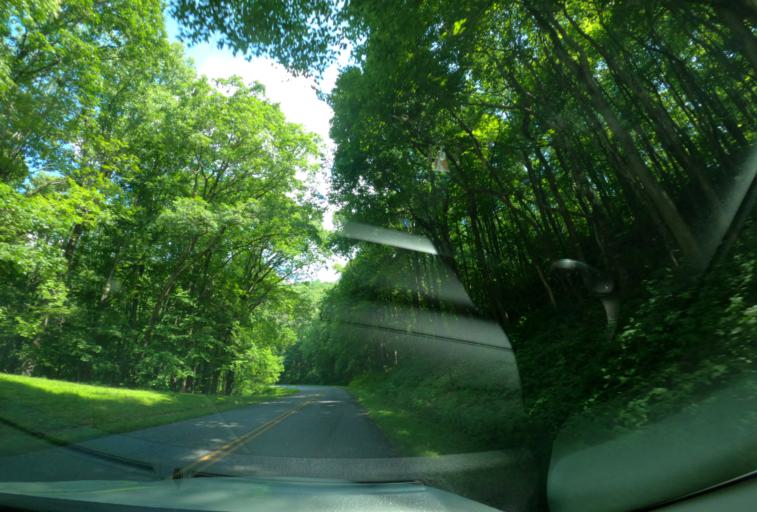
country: US
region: North Carolina
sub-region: Haywood County
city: Maggie Valley
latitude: 35.4422
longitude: -83.0880
